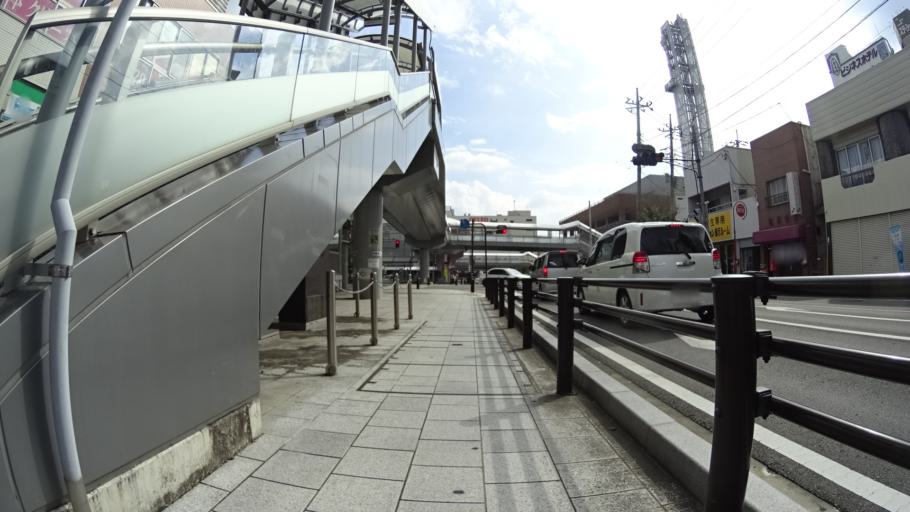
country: JP
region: Yamanashi
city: Kofu-shi
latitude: 35.6689
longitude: 138.5694
